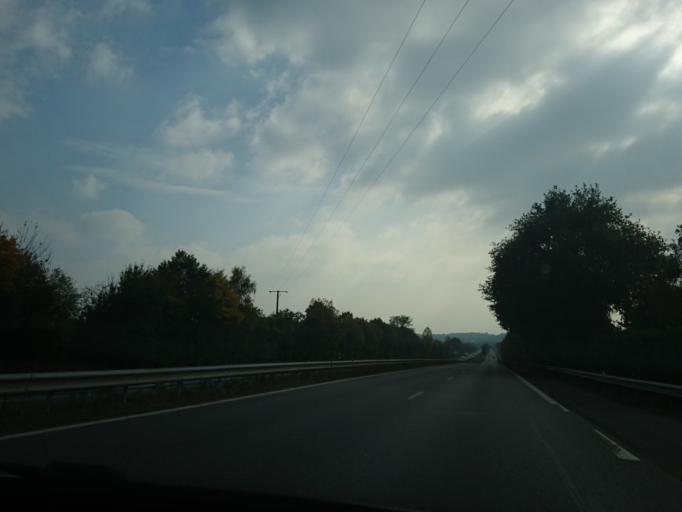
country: FR
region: Brittany
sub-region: Departement d'Ille-et-Vilaine
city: Bain-de-Bretagne
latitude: 47.8206
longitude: -1.6891
